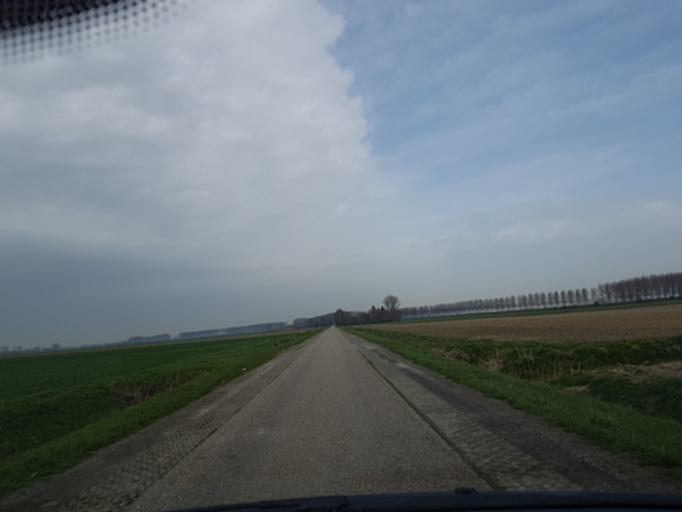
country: BE
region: Flanders
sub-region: Provincie Oost-Vlaanderen
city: Sint-Gillis-Waas
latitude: 51.2951
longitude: 4.1393
